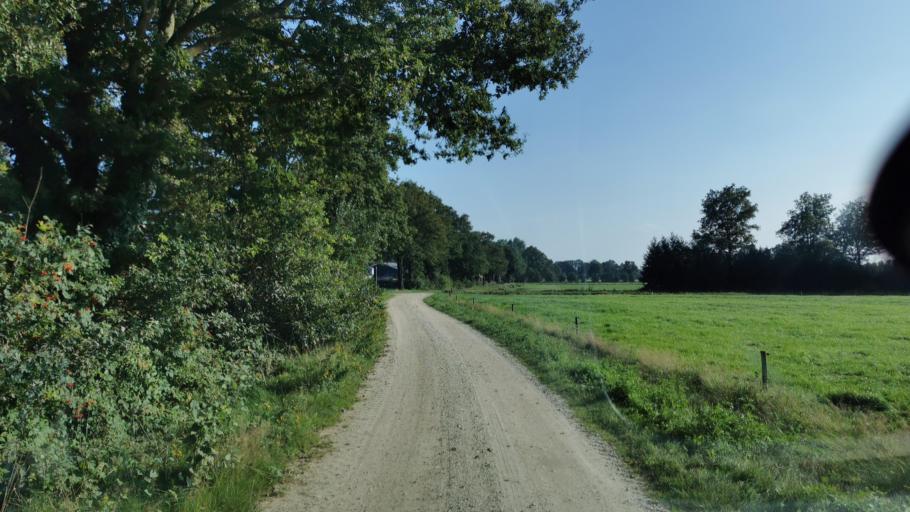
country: NL
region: Overijssel
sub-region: Gemeente Tubbergen
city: Tubbergen
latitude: 52.3701
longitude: 6.8631
